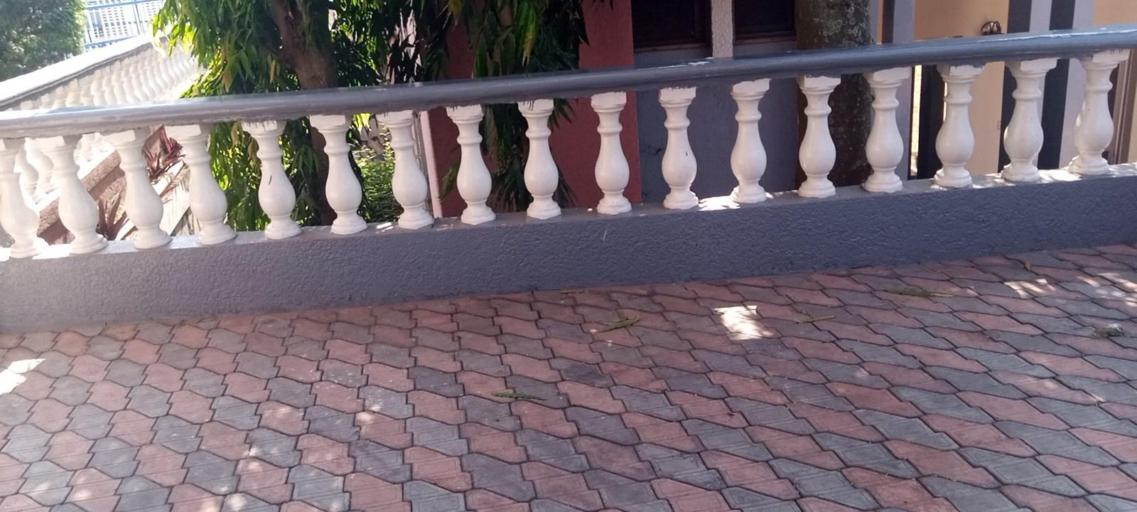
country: CD
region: Kasai-Oriental
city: Mbuji-Mayi
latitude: -6.1242
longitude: 23.5943
